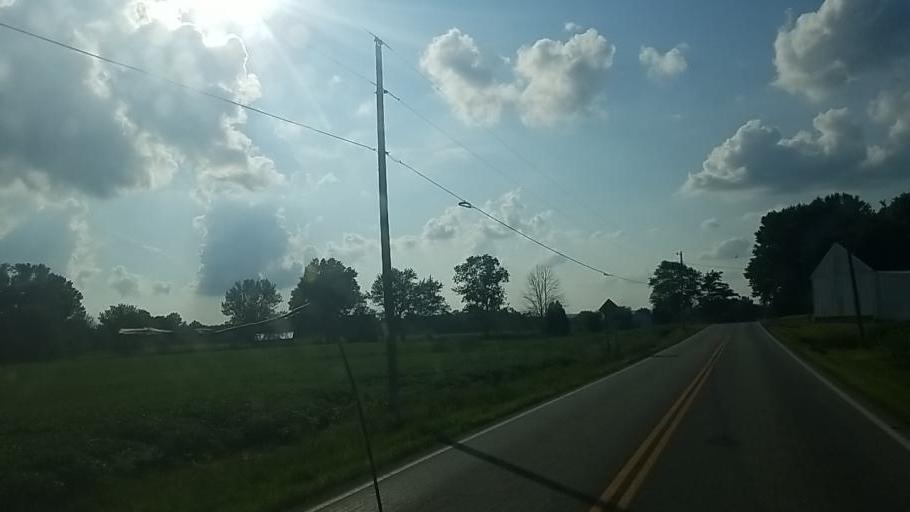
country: US
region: Ohio
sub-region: Wayne County
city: West Salem
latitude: 40.8796
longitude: -82.1100
